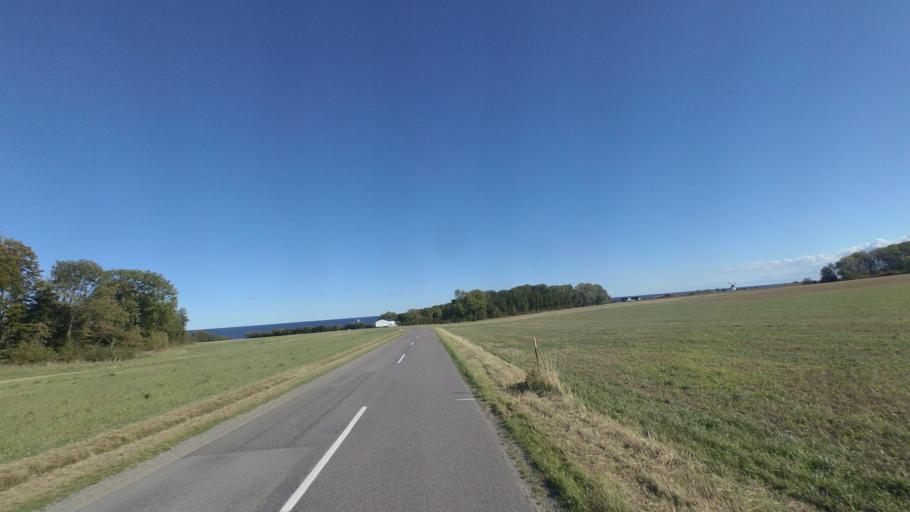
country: DK
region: Capital Region
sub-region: Bornholm Kommune
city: Nexo
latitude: 55.1104
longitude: 15.1331
